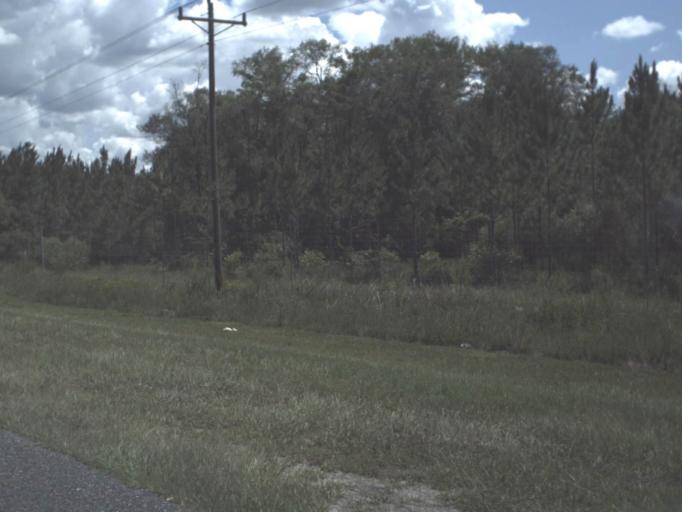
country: US
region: Florida
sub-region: Taylor County
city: Steinhatchee
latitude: 29.8043
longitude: -83.3410
